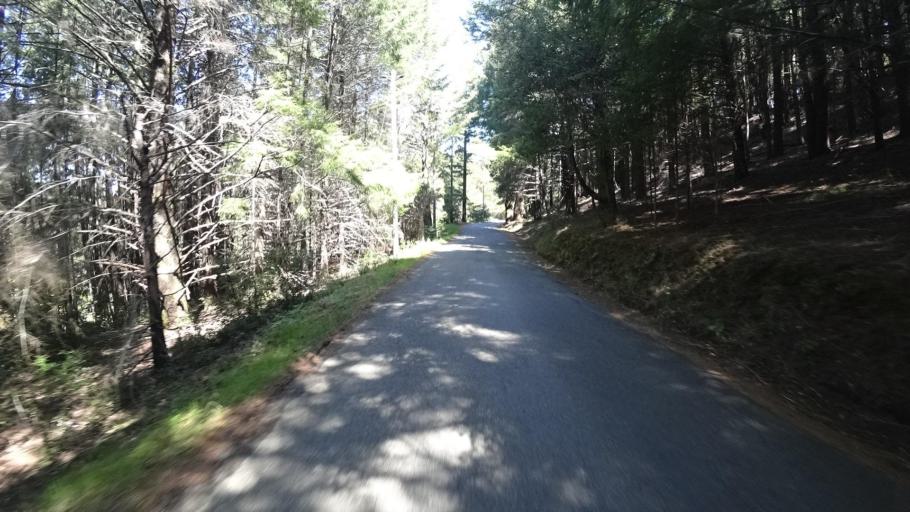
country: US
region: California
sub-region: Humboldt County
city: Redway
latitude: 40.1116
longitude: -123.9615
